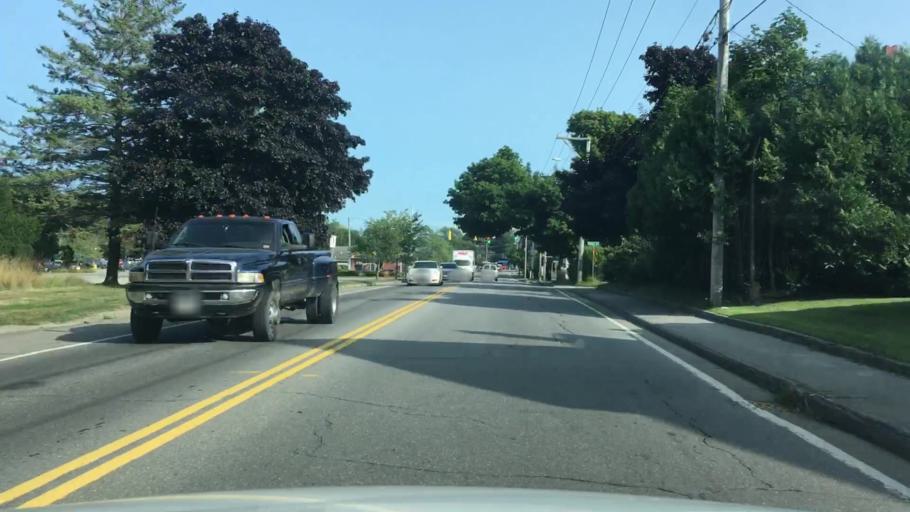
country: US
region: Maine
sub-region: Knox County
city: Rockland
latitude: 44.1175
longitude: -69.1084
